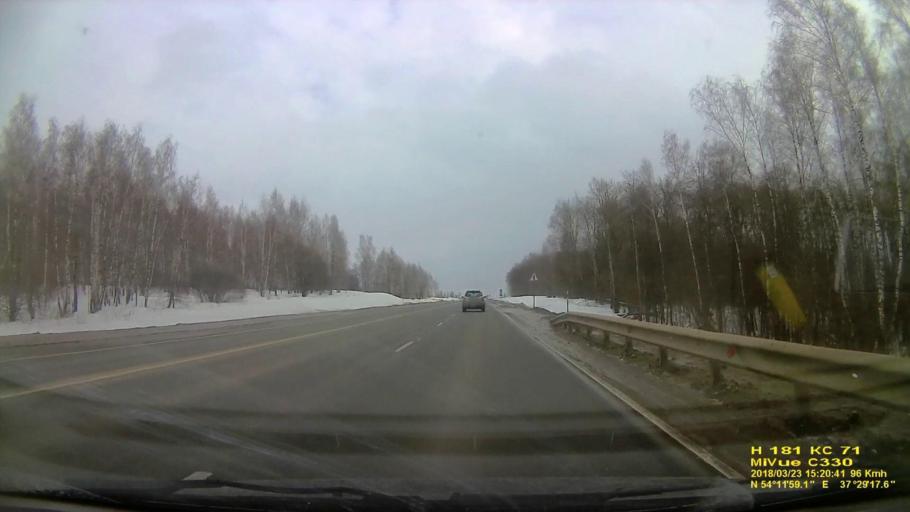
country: RU
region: Tula
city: Barsuki
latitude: 54.1998
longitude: 37.4882
